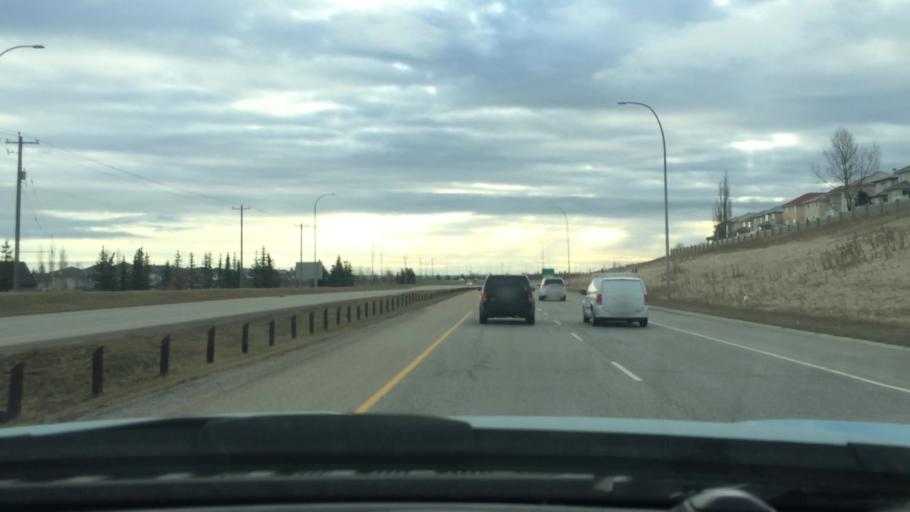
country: CA
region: Alberta
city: Calgary
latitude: 51.1460
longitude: -114.1314
